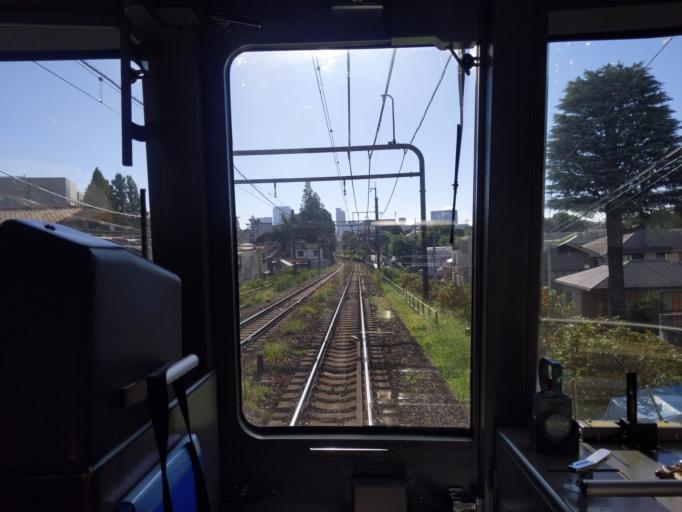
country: JP
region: Tokyo
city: Tokyo
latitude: 35.6600
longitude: 139.6754
